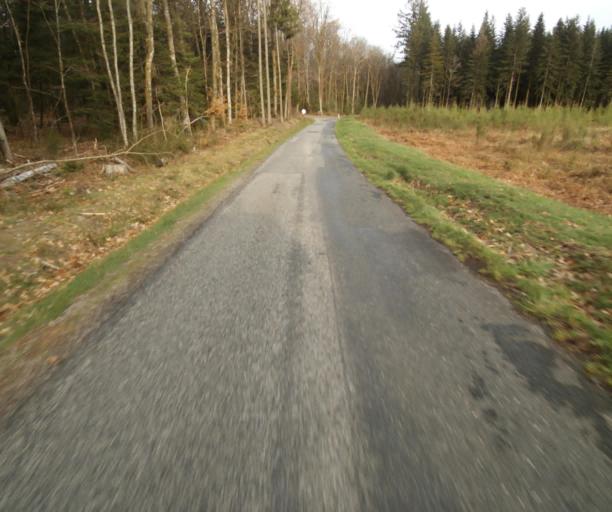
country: FR
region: Limousin
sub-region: Departement de la Correze
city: Argentat
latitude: 45.2212
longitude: 1.9421
